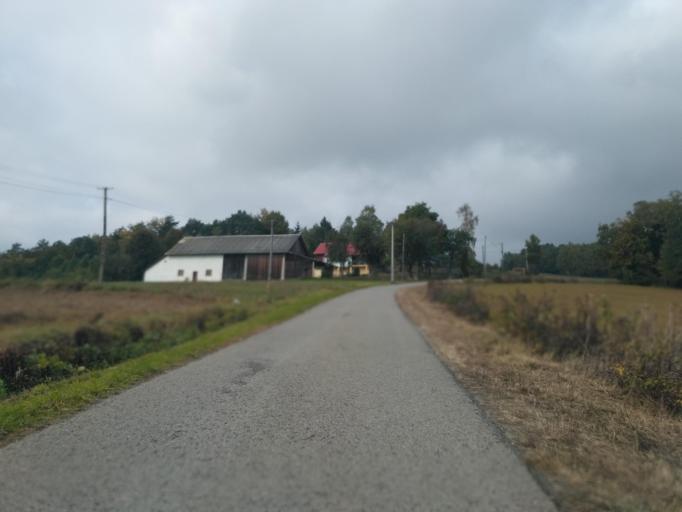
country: PL
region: Subcarpathian Voivodeship
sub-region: Powiat debicki
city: Brzostek
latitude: 49.9454
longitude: 21.4475
